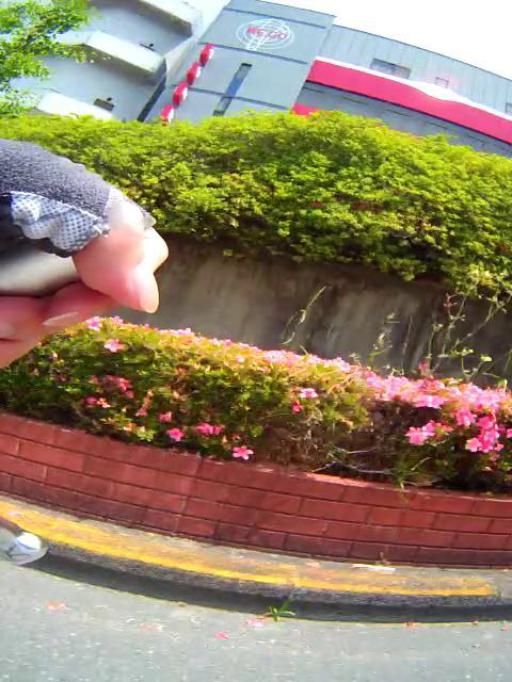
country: JP
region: Osaka
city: Mino
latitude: 34.8240
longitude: 135.4894
